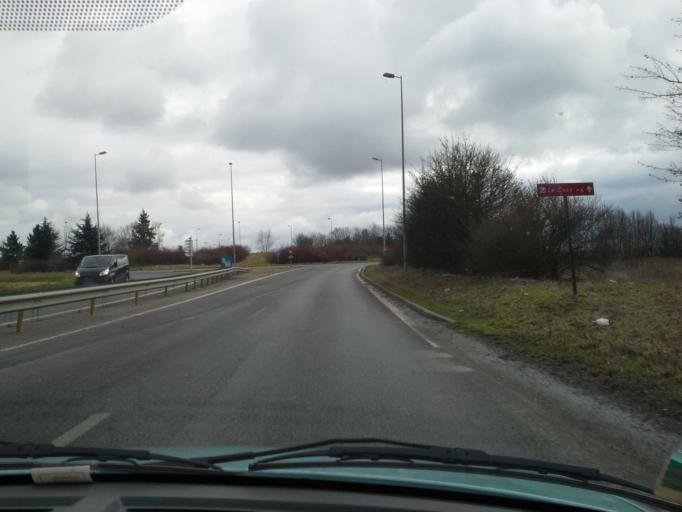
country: FR
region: Centre
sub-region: Departement du Loir-et-Cher
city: Villebarou
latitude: 47.6252
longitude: 1.2928
